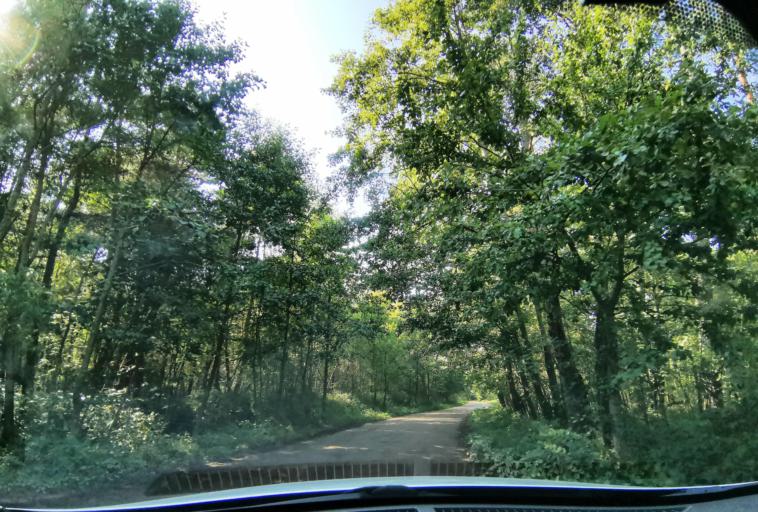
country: LT
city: Nida
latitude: 55.1617
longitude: 20.8273
